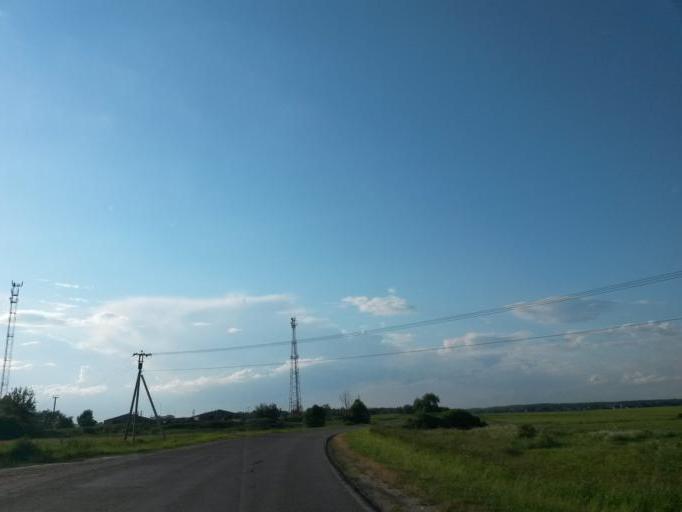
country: RU
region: Moskovskaya
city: Lyubuchany
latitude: 55.2339
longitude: 37.6447
